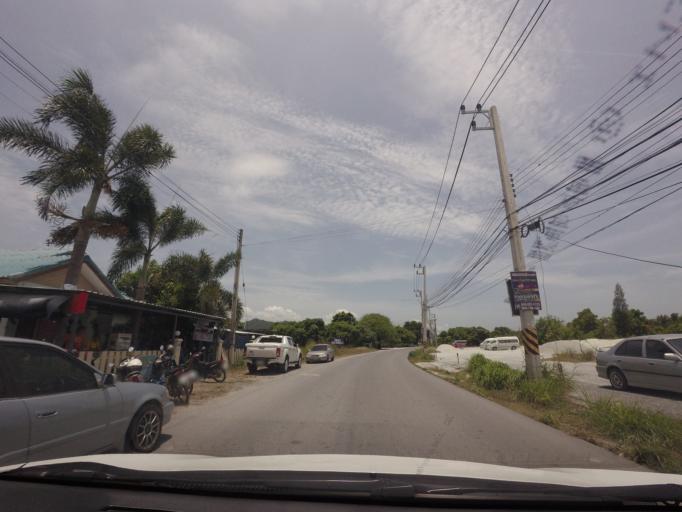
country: TH
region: Chon Buri
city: Chon Buri
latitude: 13.2953
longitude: 100.9743
